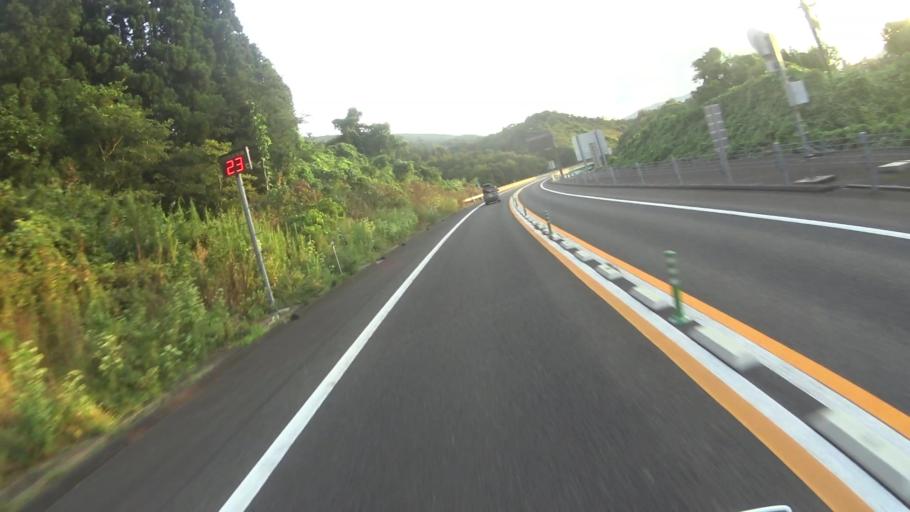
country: JP
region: Kyoto
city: Miyazu
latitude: 35.5100
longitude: 135.1928
